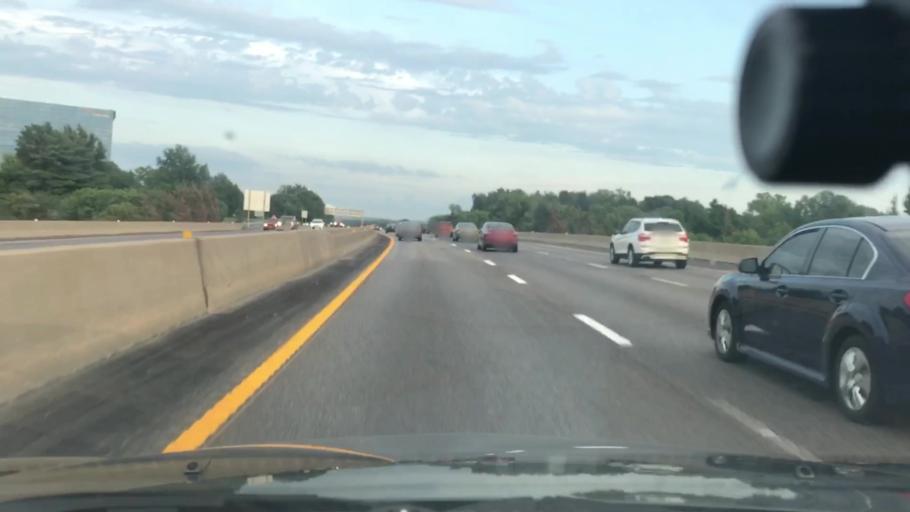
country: US
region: Missouri
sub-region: Saint Louis County
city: Chesterfield
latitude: 38.6532
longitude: -90.5591
